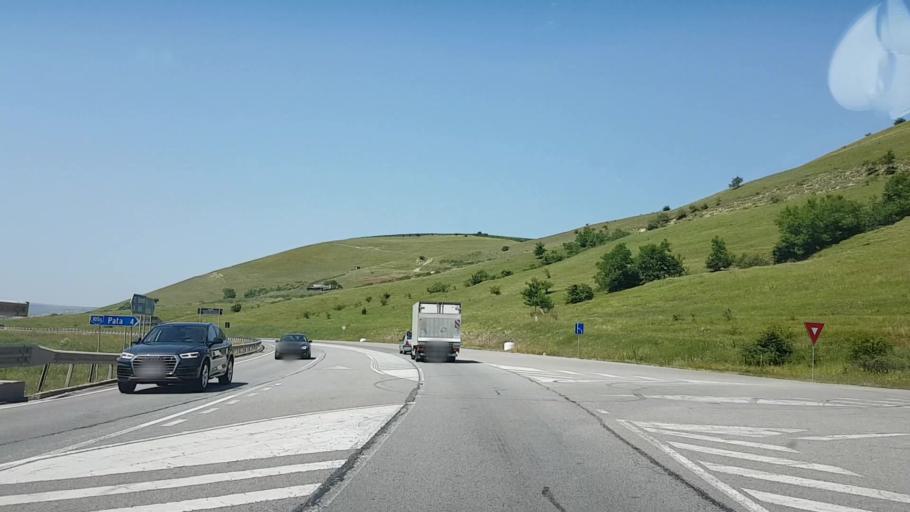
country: RO
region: Cluj
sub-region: Comuna Apahida
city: Dezmir
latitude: 46.7456
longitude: 23.7120
